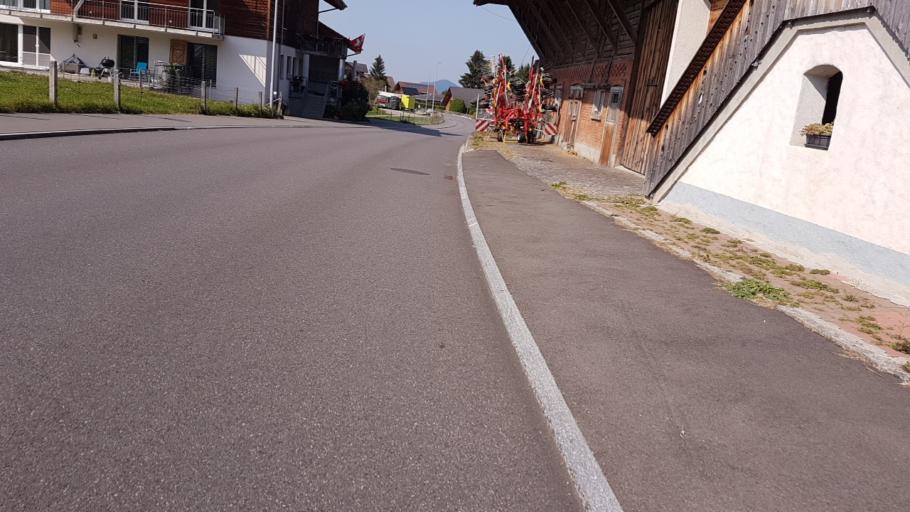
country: CH
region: Bern
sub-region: Frutigen-Niedersimmental District
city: Aeschi
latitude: 46.6549
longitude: 7.7000
